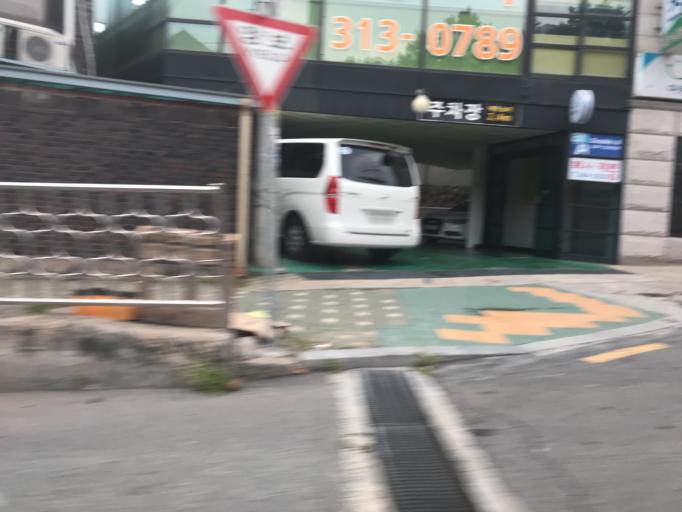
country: KR
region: Seoul
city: Seoul
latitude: 37.5673
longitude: 126.9472
